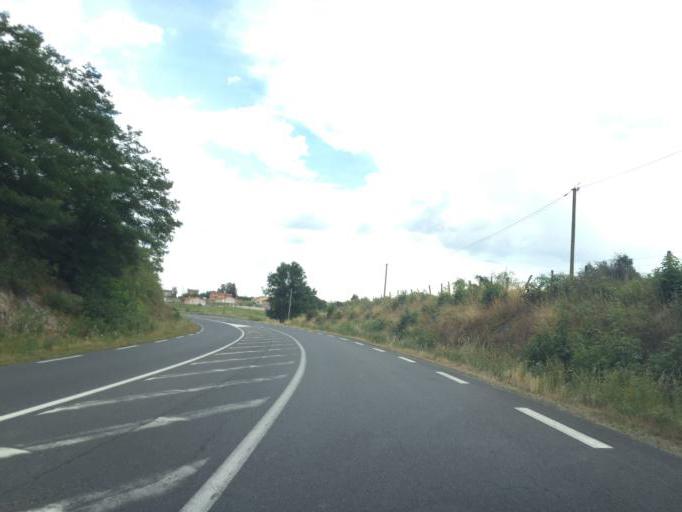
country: FR
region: Rhone-Alpes
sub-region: Departement de la Loire
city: Saint-Symphorien-de-Lay
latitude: 45.9524
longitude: 4.1931
